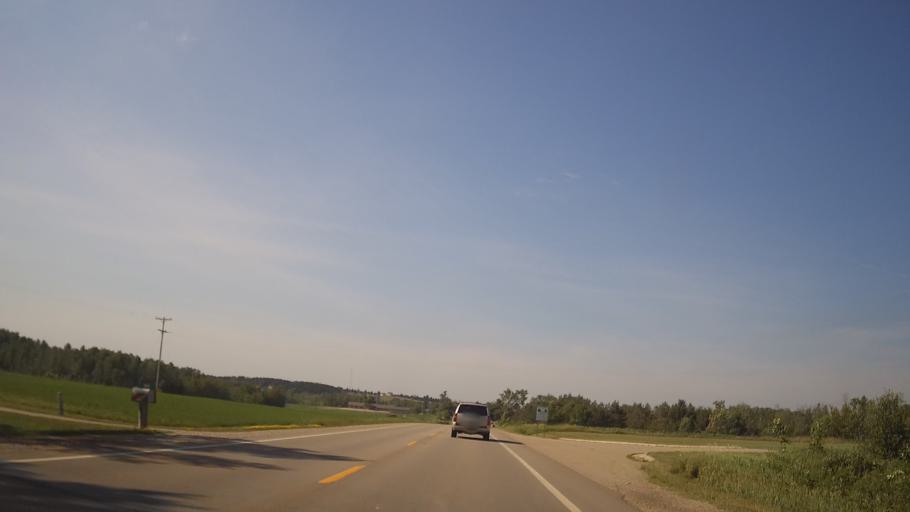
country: US
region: Michigan
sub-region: Ogemaw County
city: West Branch
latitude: 44.2839
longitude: -84.1257
